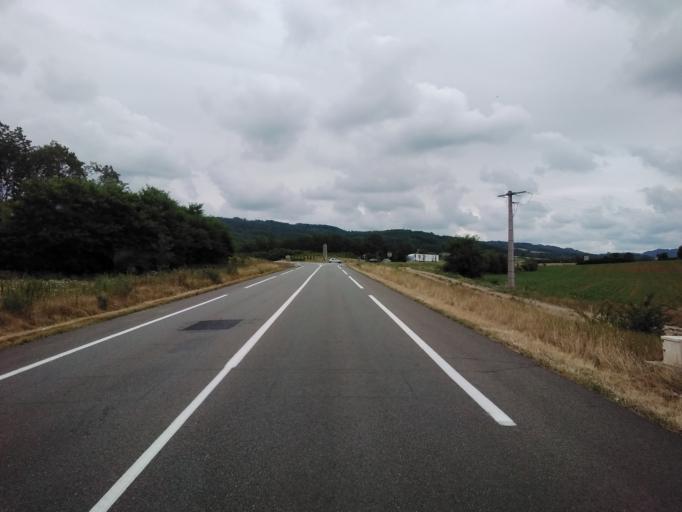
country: FR
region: Franche-Comte
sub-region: Departement du Jura
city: Montmorot
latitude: 46.6541
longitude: 5.5083
